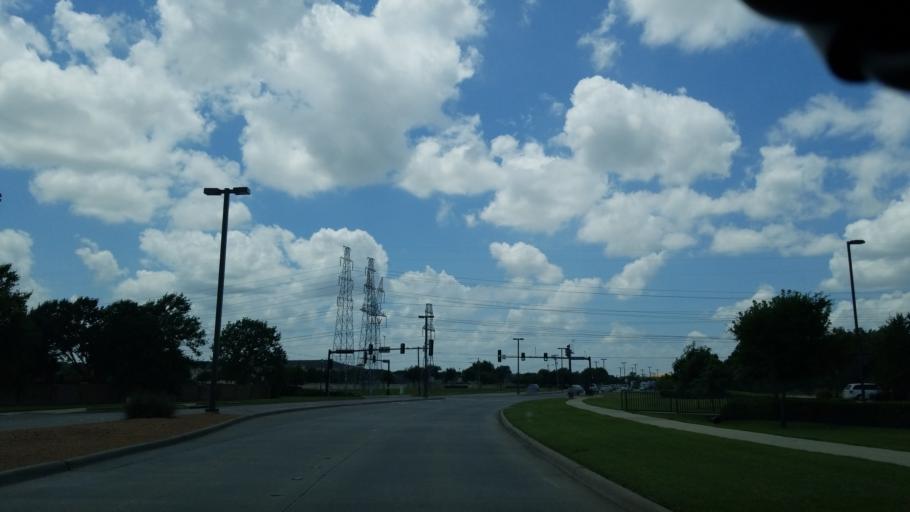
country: US
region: Texas
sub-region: Dallas County
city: Carrollton
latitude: 32.9662
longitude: -96.9501
